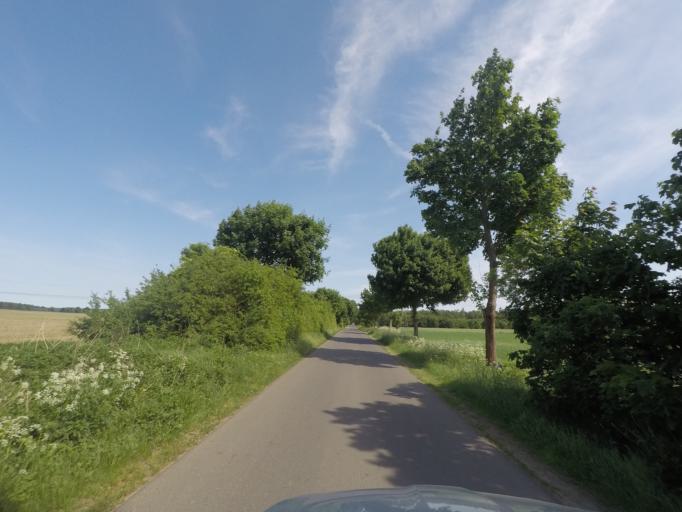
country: DE
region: Brandenburg
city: Britz
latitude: 52.8911
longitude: 13.7908
